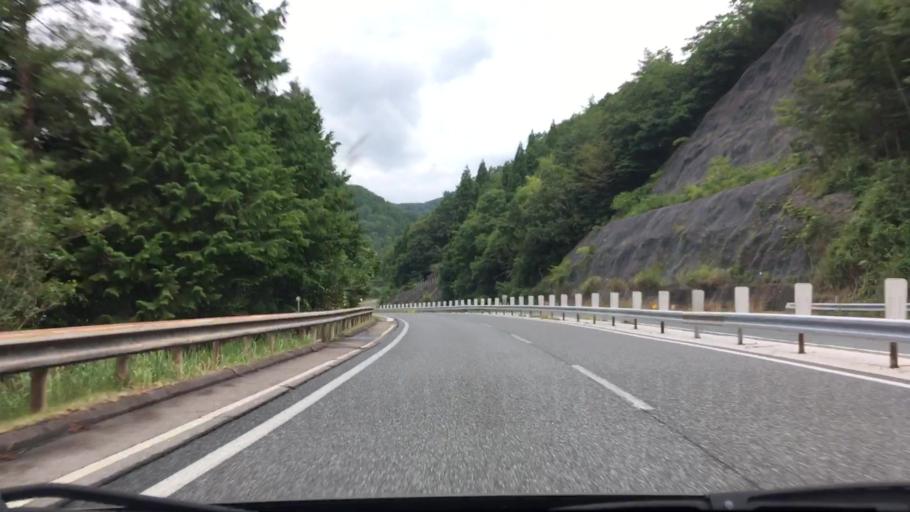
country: JP
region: Okayama
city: Niimi
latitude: 35.0098
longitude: 133.5058
